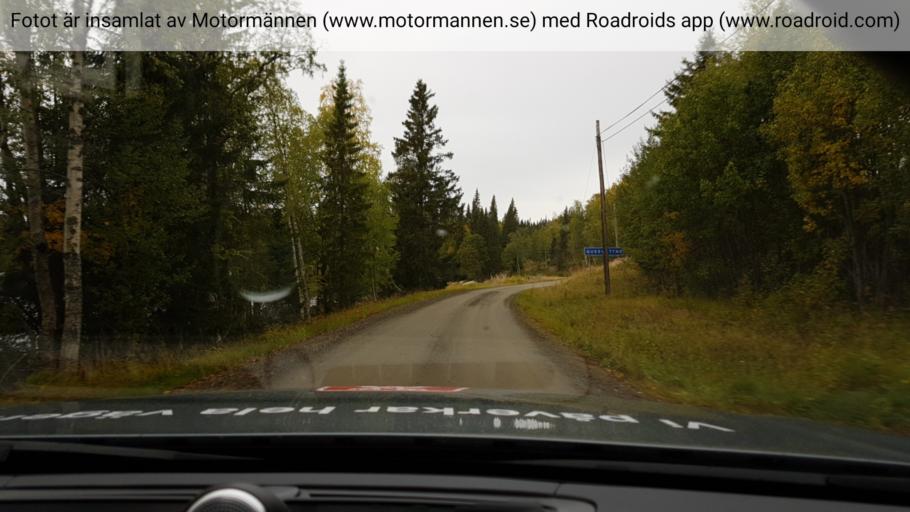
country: NO
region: Nord-Trondelag
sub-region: Lierne
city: Sandvika
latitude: 64.4676
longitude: 14.2902
